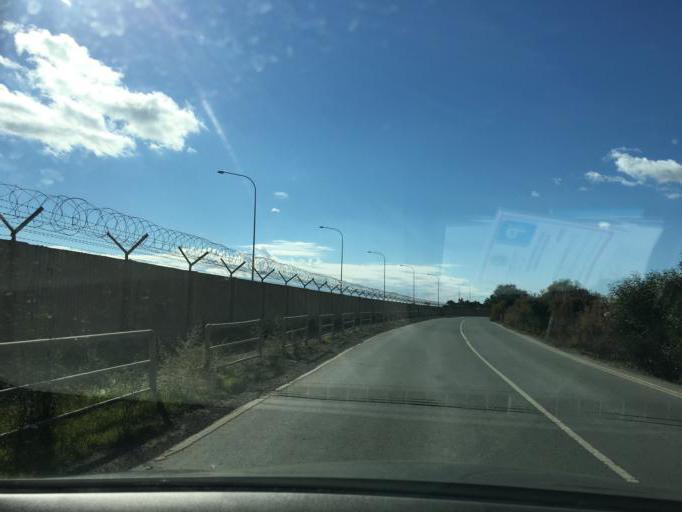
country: CY
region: Limassol
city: Limassol
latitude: 34.6483
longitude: 33.0063
